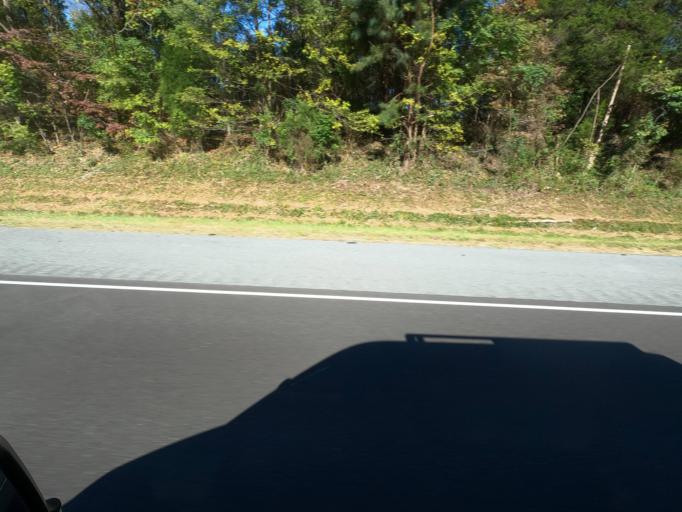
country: US
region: Tennessee
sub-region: Williamson County
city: Fairview
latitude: 36.0307
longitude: -87.1713
